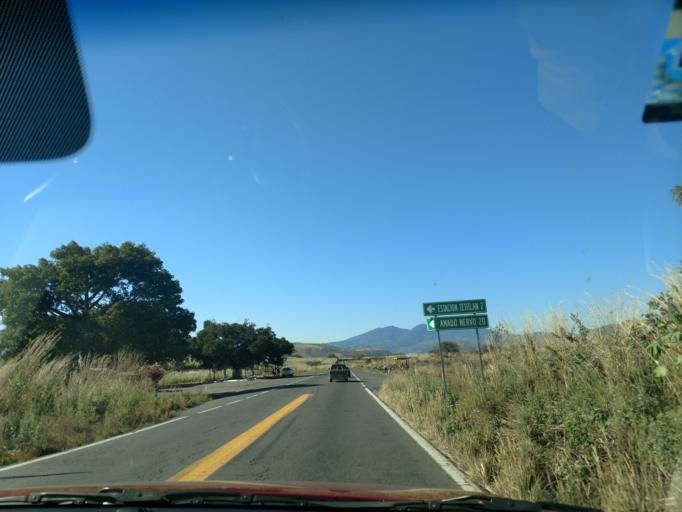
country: MX
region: Nayarit
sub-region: Ahuacatlan
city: Ahuacatlan
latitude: 21.1290
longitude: -104.6015
